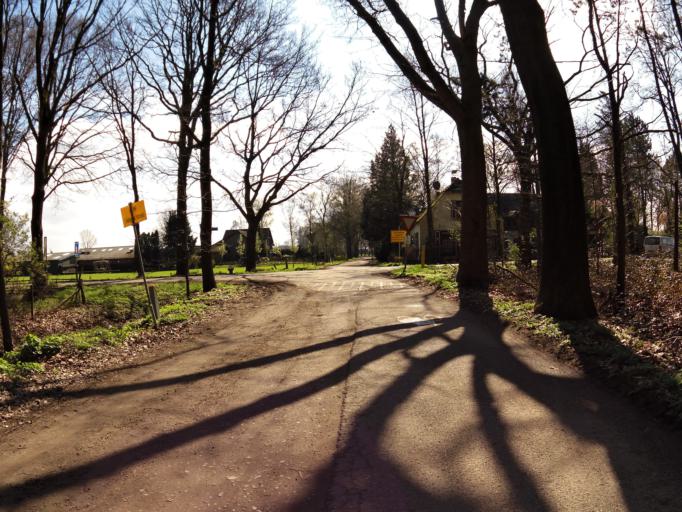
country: NL
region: North Brabant
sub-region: Gemeente Vught
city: Vught
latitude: 51.6212
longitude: 5.2732
